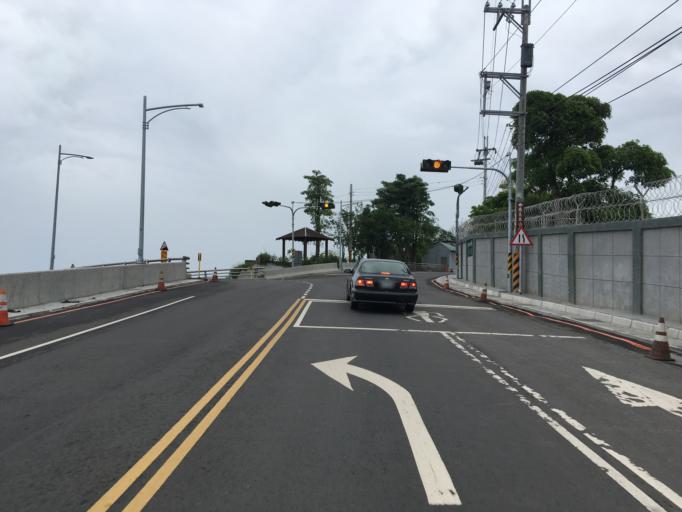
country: TW
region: Taiwan
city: Fengyuan
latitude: 24.2062
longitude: 120.7920
